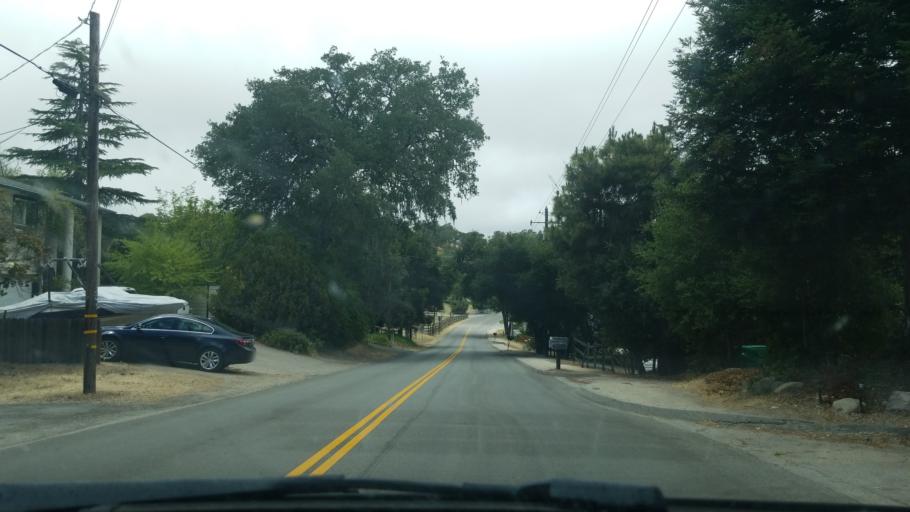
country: US
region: California
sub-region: San Luis Obispo County
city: Atascadero
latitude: 35.4623
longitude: -120.6619
